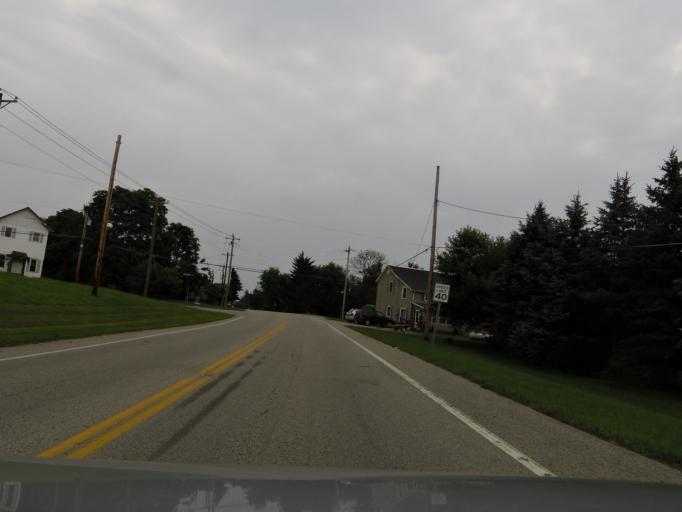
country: US
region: Ohio
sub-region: Clinton County
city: Blanchester
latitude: 39.2815
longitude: -83.9114
